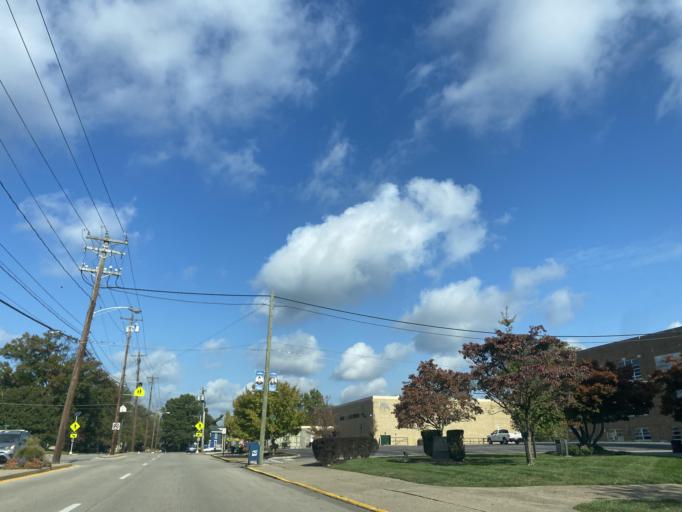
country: US
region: Kentucky
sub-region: Campbell County
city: Fort Thomas
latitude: 39.0724
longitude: -84.4462
